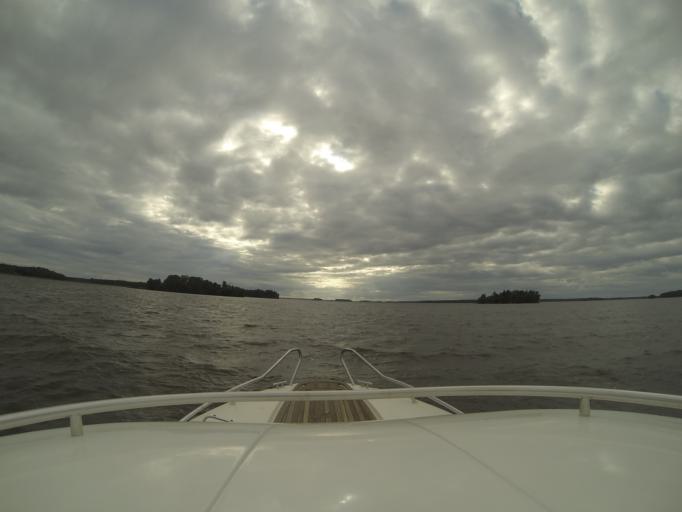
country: SE
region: Soedermanland
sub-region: Eskilstuna Kommun
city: Kvicksund
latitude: 59.4524
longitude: 16.2988
